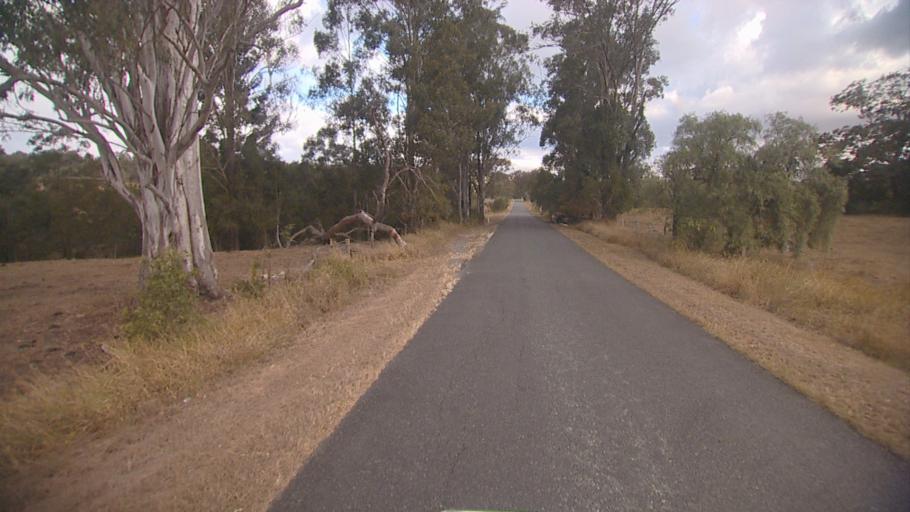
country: AU
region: Queensland
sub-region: Logan
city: Cedar Vale
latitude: -27.8928
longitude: 153.0654
